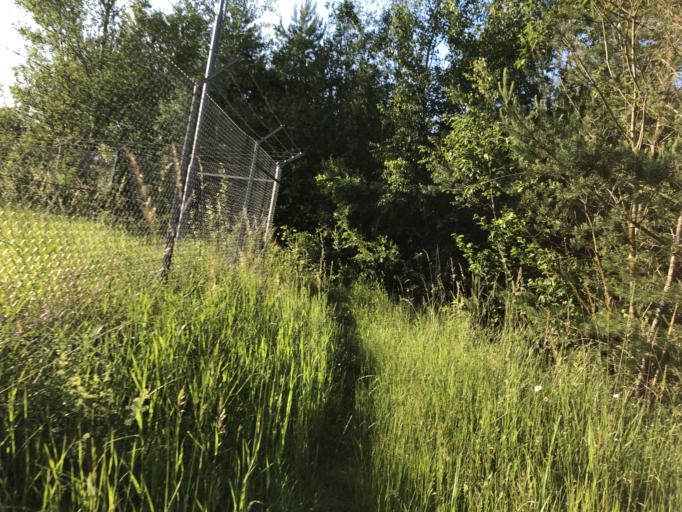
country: DE
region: Bavaria
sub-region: Upper Franconia
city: Memmelsdorf
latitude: 49.9140
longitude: 10.9455
